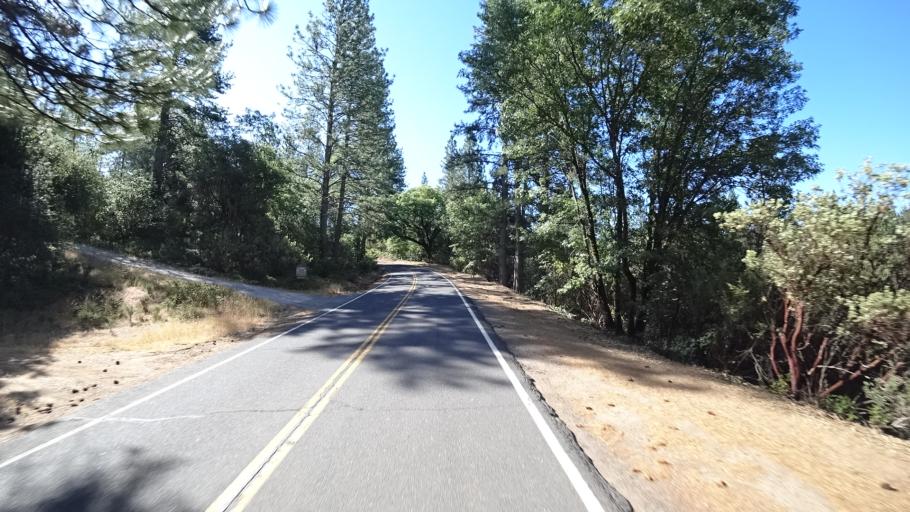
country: US
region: California
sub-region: Amador County
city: Pioneer
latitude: 38.3742
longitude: -120.4773
